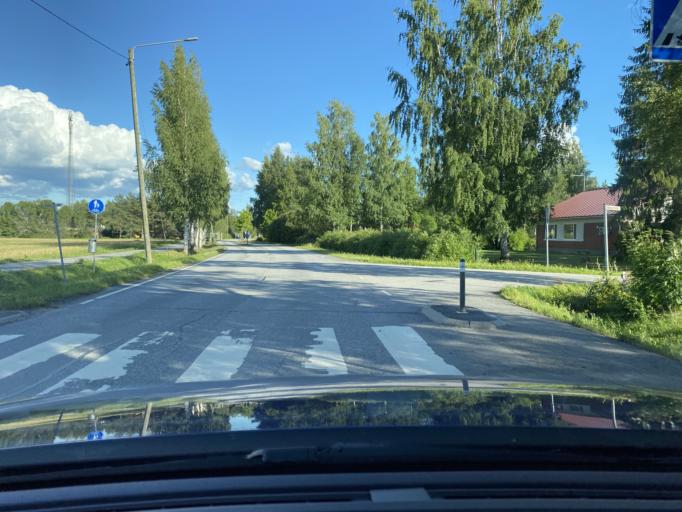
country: FI
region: Ostrobothnia
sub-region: Kyroenmaa
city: Laihia
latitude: 62.9788
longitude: 21.9984
